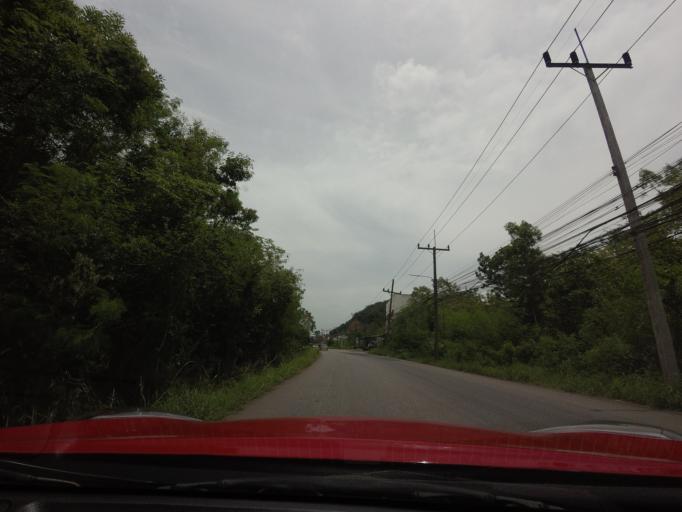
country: TH
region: Songkhla
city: Hat Yai
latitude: 6.9999
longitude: 100.5174
